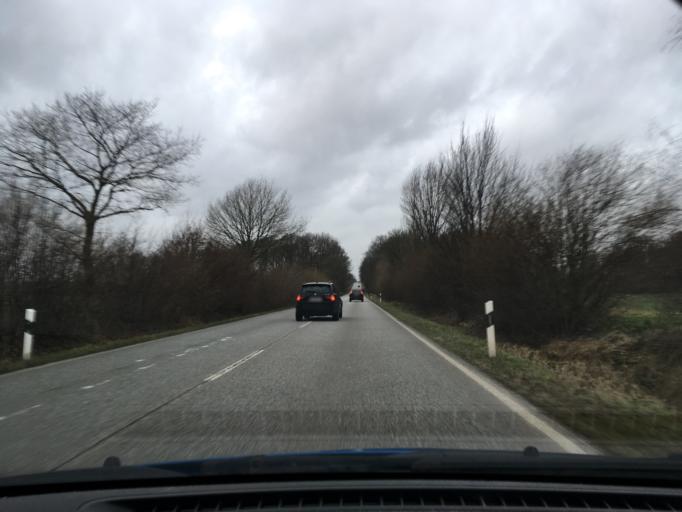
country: DE
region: Schleswig-Holstein
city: Wangelau
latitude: 53.4588
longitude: 10.5476
